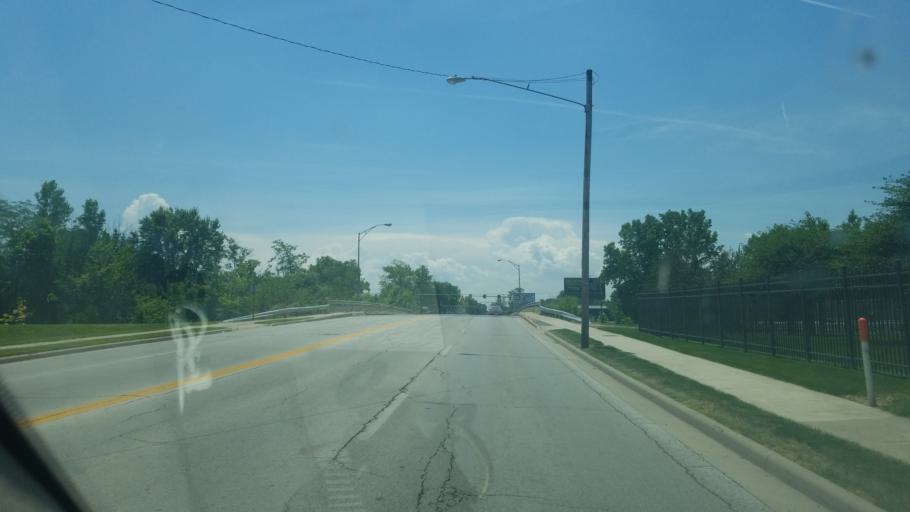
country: US
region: Ohio
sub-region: Hancock County
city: Findlay
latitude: 41.0415
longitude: -83.6413
